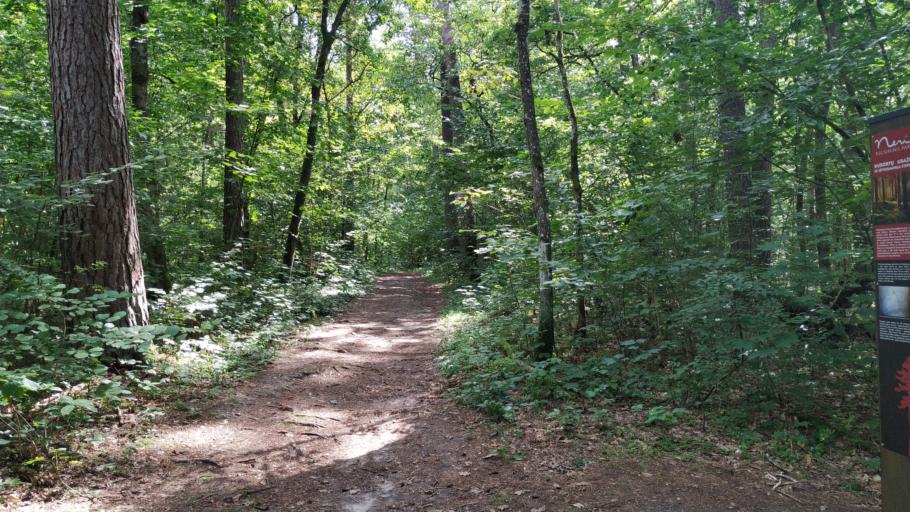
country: LT
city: Grigiskes
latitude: 54.8099
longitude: 24.9700
